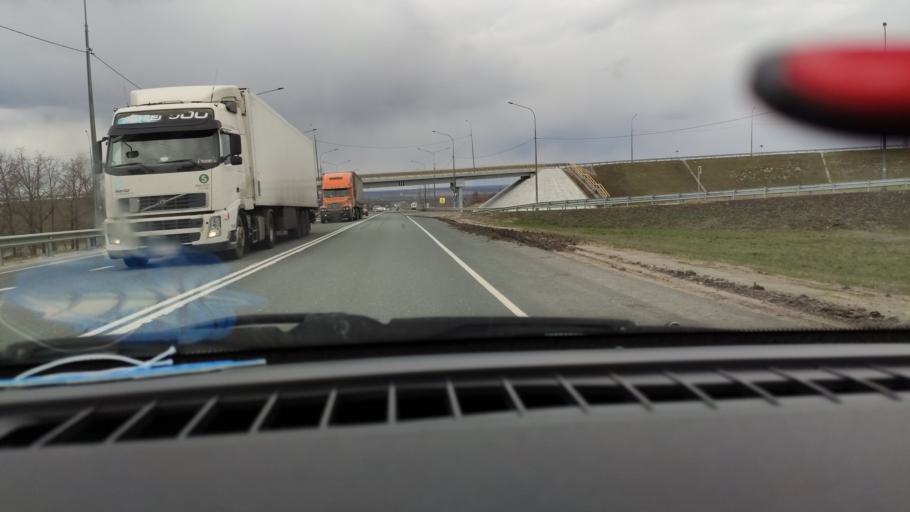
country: RU
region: Saratov
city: Yelshanka
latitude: 51.8256
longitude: 46.2891
